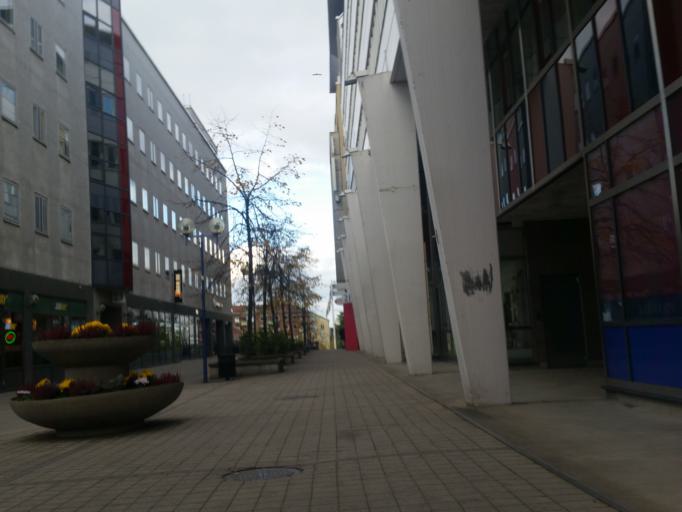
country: SE
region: Stockholm
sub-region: Stockholms Kommun
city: Arsta
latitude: 59.2957
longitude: 18.0806
